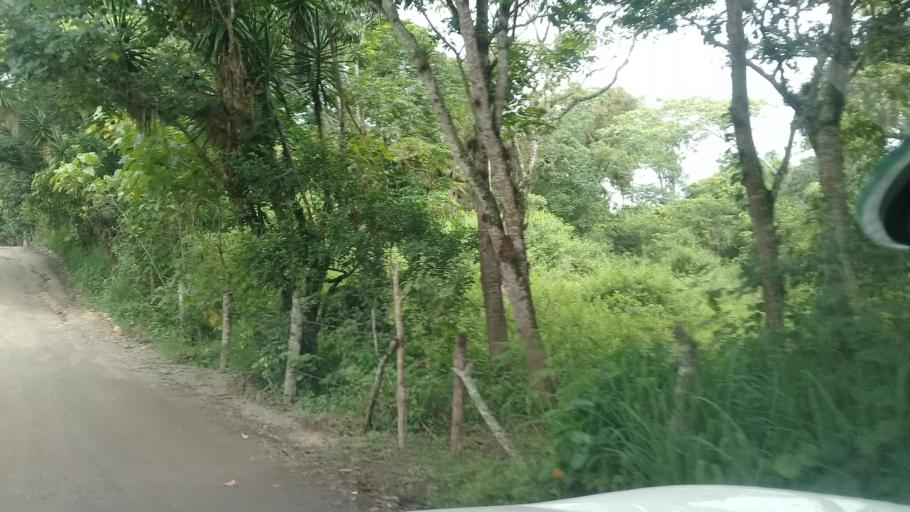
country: MX
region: Veracruz
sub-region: Emiliano Zapata
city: Jacarandas
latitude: 19.4810
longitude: -96.8536
